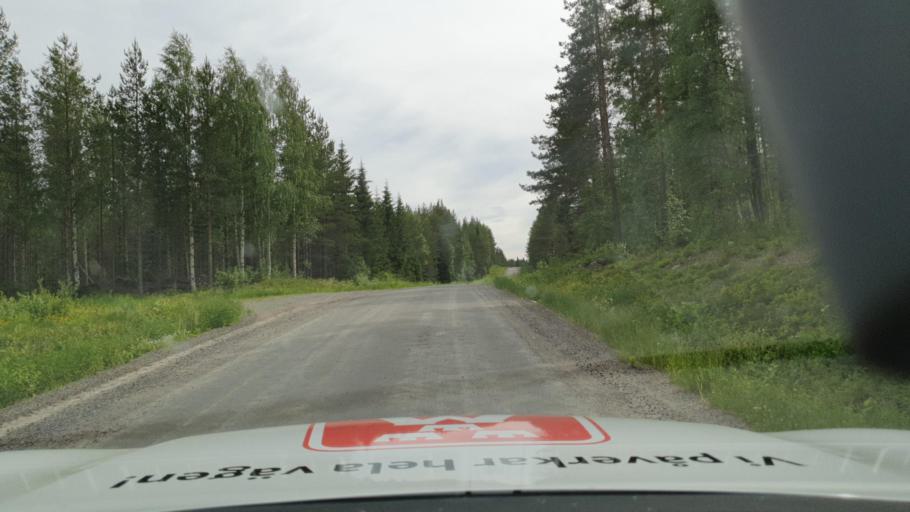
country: SE
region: Vaesterbotten
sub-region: Skelleftea Kommun
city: Burea
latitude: 64.4266
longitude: 21.0133
